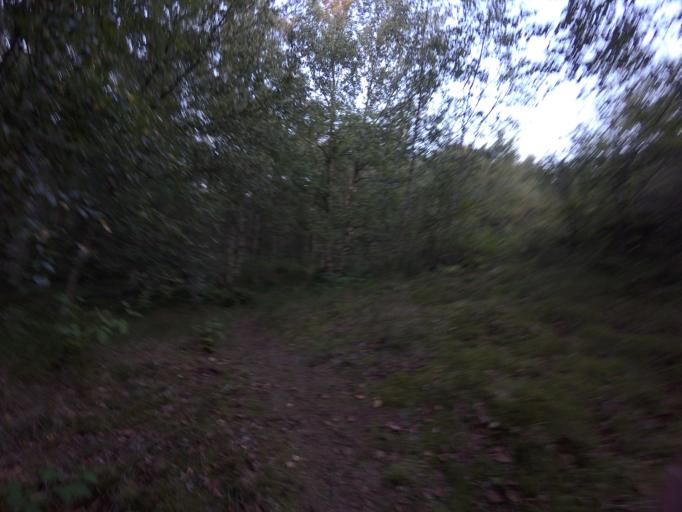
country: NL
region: Friesland
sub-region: Gemeente Schiermonnikoog
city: Schiermonnikoog
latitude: 53.4906
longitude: 6.1704
